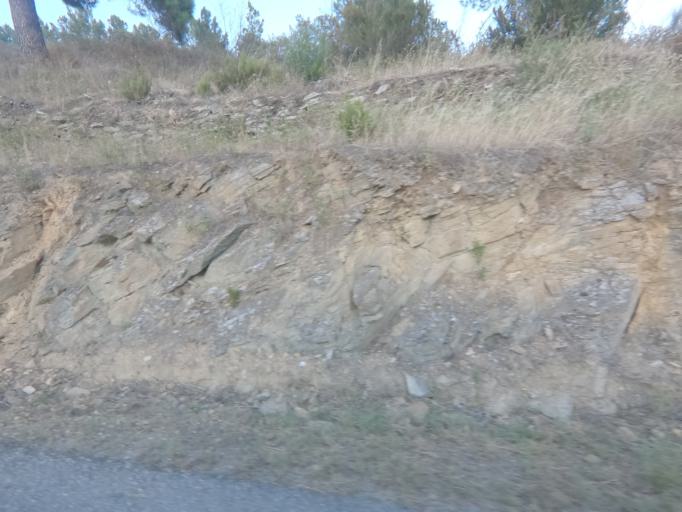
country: PT
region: Viseu
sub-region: Armamar
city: Armamar
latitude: 41.1618
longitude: -7.6819
